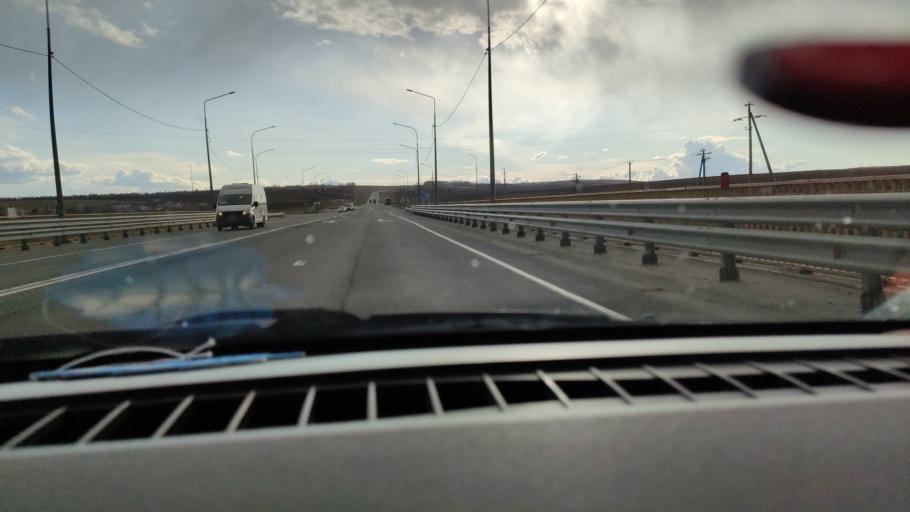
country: RU
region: Saratov
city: Yelshanka
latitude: 51.8245
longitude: 46.3845
